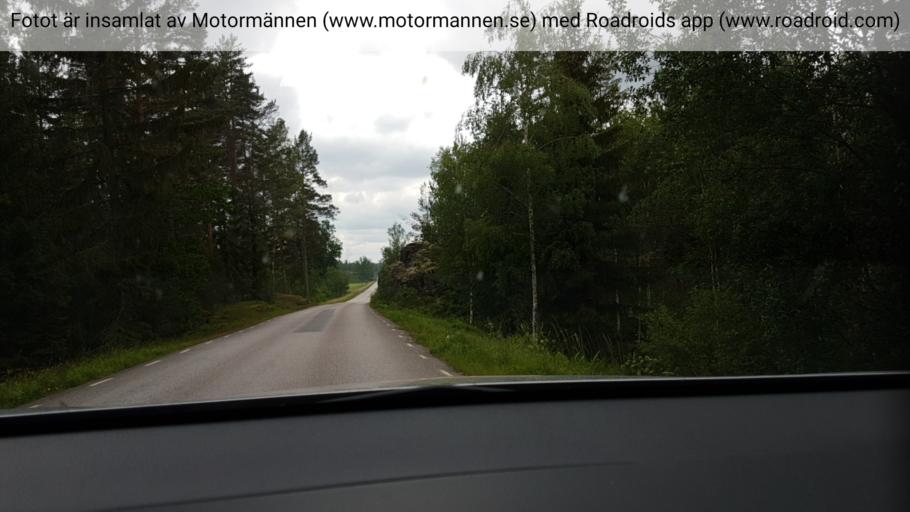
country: SE
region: OEstergoetland
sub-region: Valdemarsviks Kommun
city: Valdemarsvik
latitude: 58.0622
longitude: 16.6334
